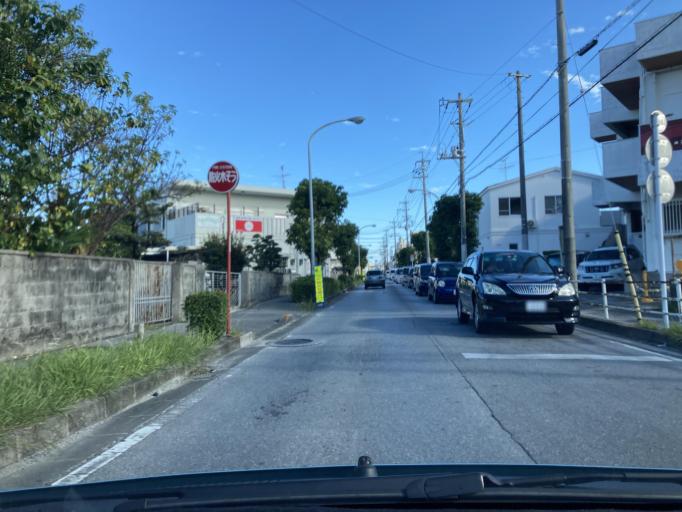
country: JP
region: Okinawa
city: Chatan
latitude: 26.3591
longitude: 127.7481
